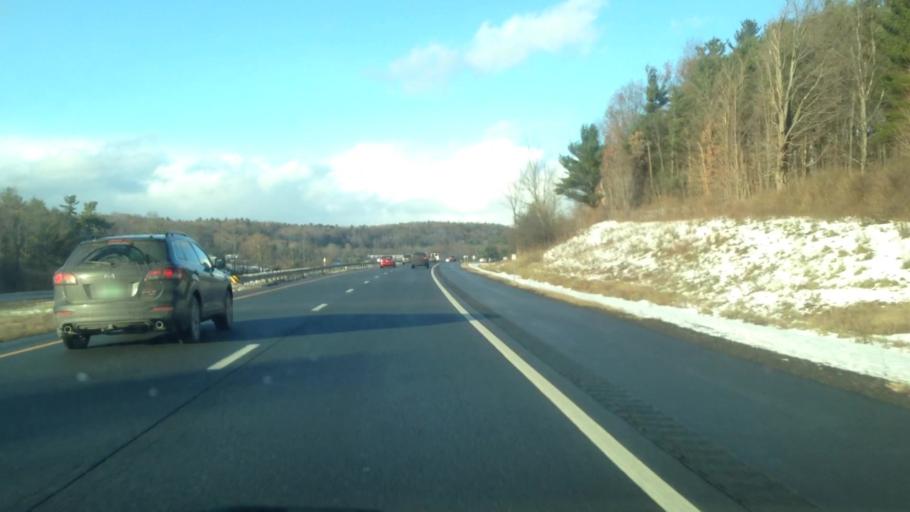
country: US
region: New York
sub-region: Schenectady County
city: Rotterdam
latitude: 42.8126
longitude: -74.0192
